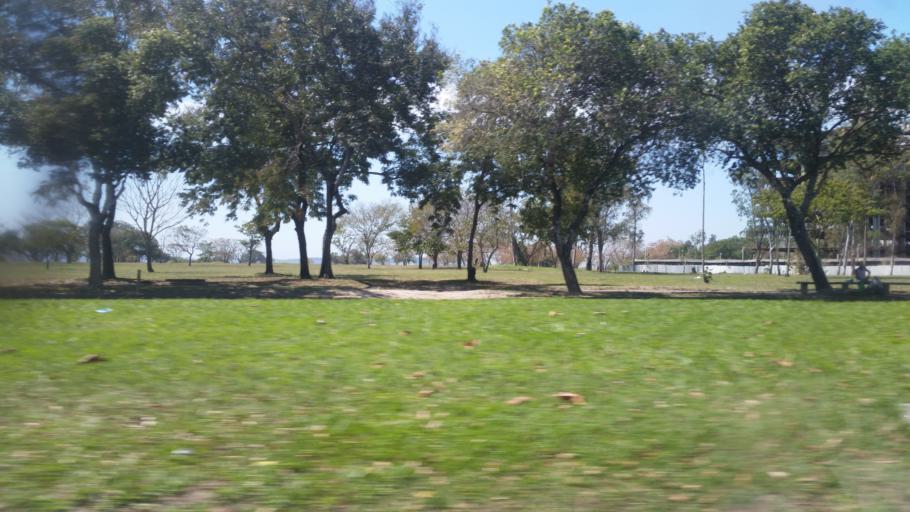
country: BR
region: Rio de Janeiro
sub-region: Rio De Janeiro
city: Rio de Janeiro
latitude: -22.8594
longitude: -43.2283
